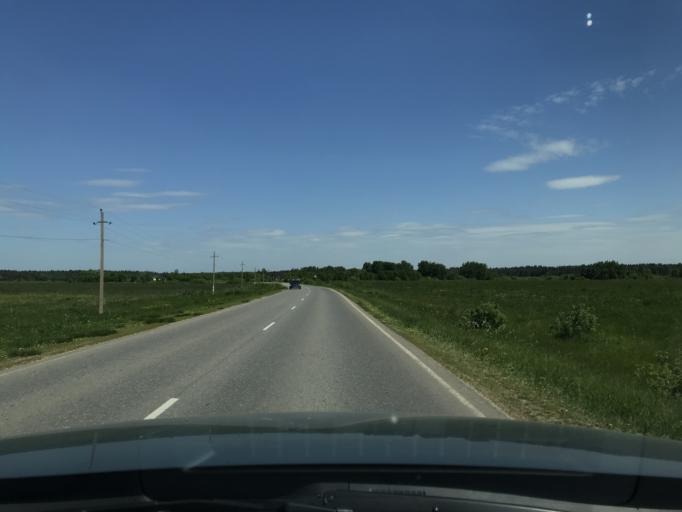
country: RU
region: Moskovskaya
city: Vereya
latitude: 55.3224
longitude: 36.2704
